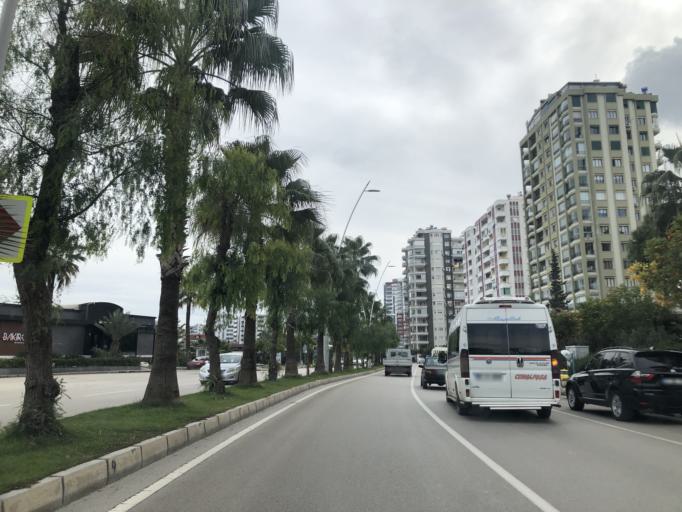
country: TR
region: Adana
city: Adana
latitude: 37.0563
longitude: 35.2867
